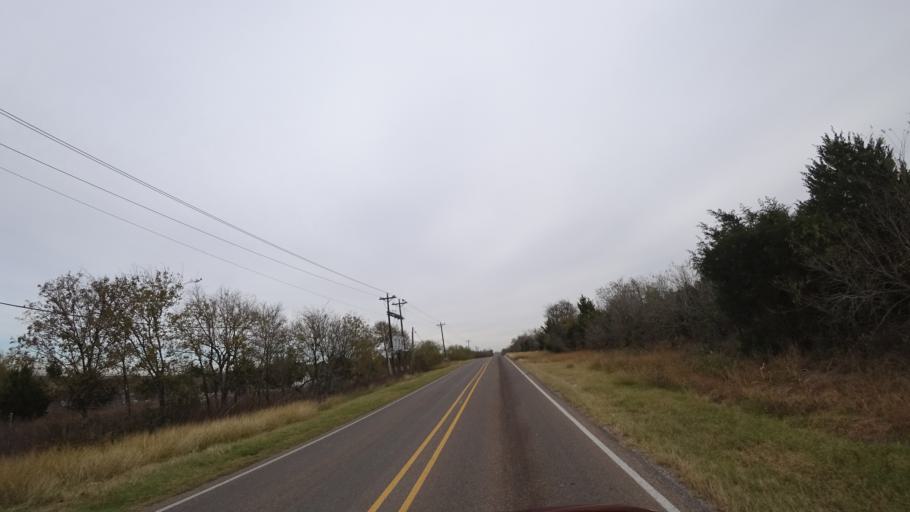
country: US
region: Texas
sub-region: Travis County
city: Garfield
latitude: 30.0994
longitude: -97.5969
